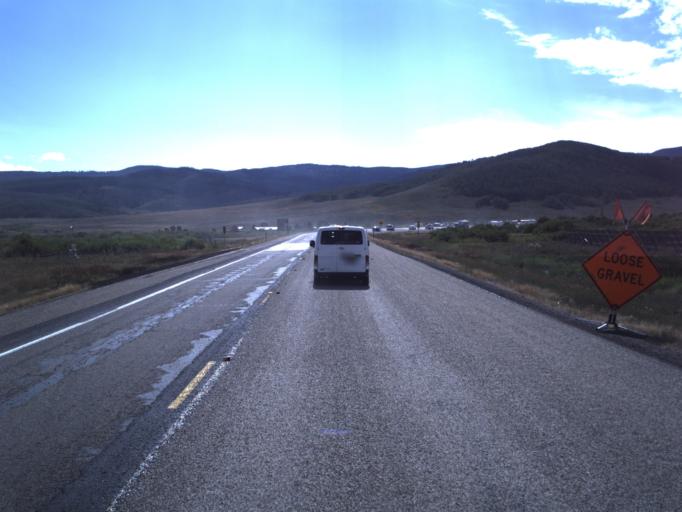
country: US
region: Utah
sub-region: Wasatch County
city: Heber
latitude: 40.2420
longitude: -111.1759
